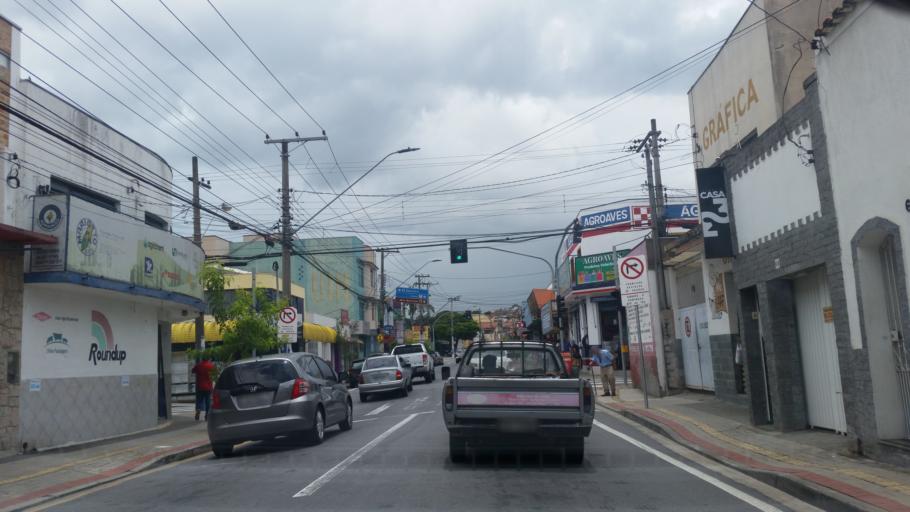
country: BR
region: Sao Paulo
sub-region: Taubate
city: Taubate
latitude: -23.0261
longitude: -45.5526
